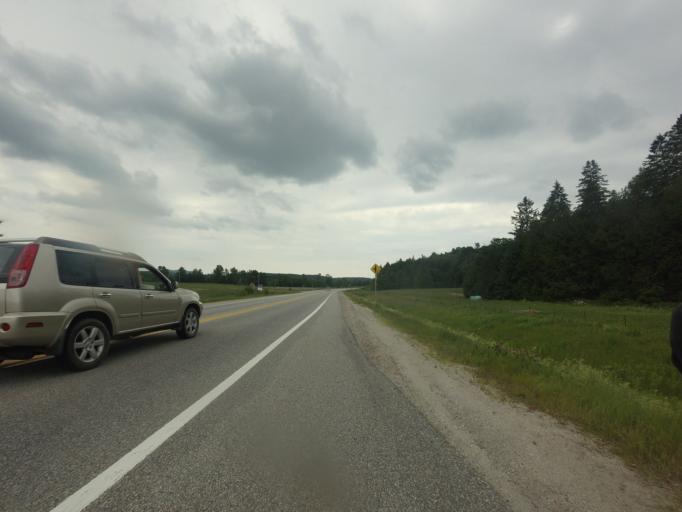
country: CA
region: Quebec
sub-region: Outaouais
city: Wakefield
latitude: 45.7257
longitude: -75.9106
